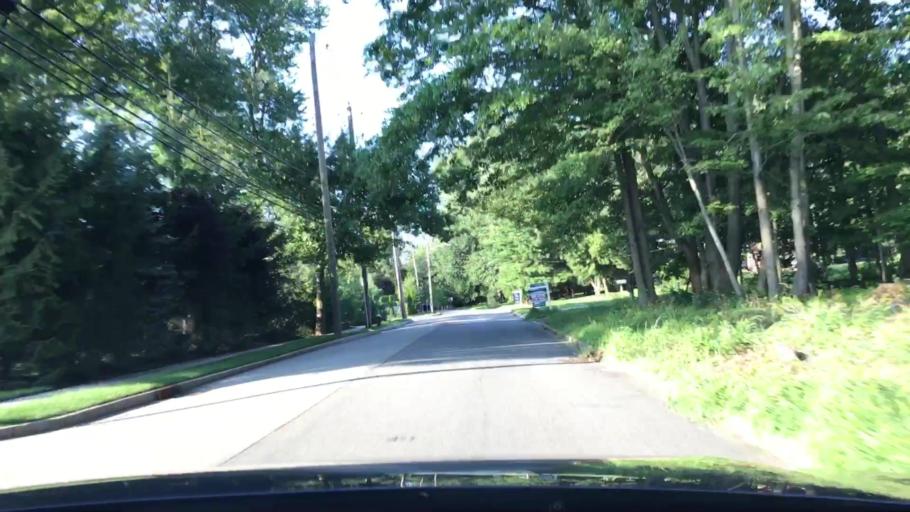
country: US
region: New Jersey
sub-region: Bergen County
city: Alpine
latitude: 40.9631
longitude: -73.9400
